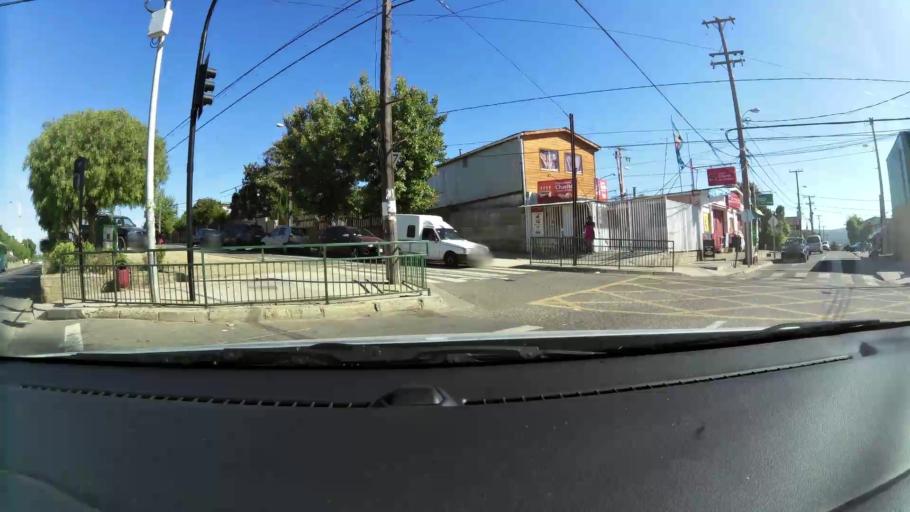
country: CL
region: Valparaiso
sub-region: Provincia de Valparaiso
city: Vina del Mar
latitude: -33.0491
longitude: -71.5610
